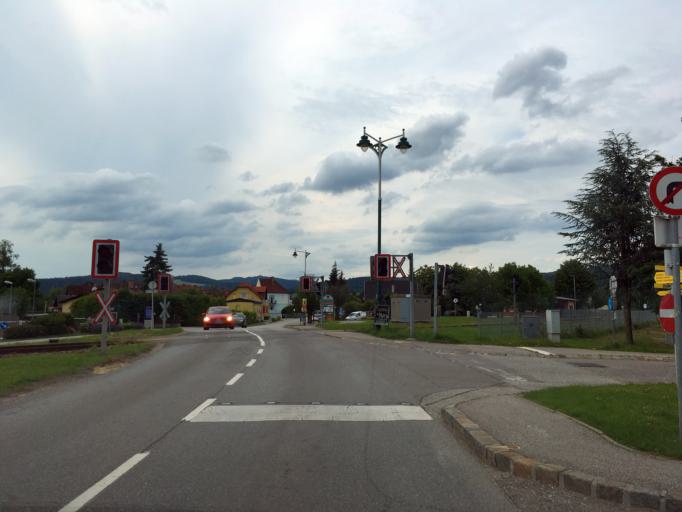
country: AT
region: Lower Austria
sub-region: Politischer Bezirk Wiener Neustadt
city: Bad Erlach
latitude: 47.7333
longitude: 16.2125
